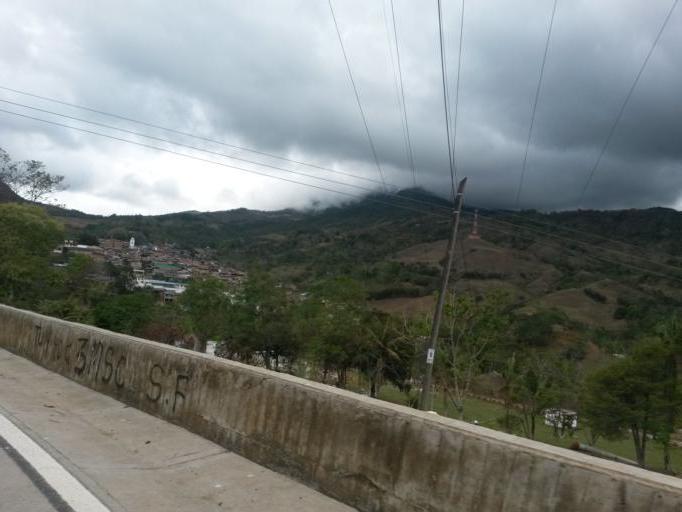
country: CO
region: Cauca
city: Almaguer
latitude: 1.8296
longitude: -76.9708
